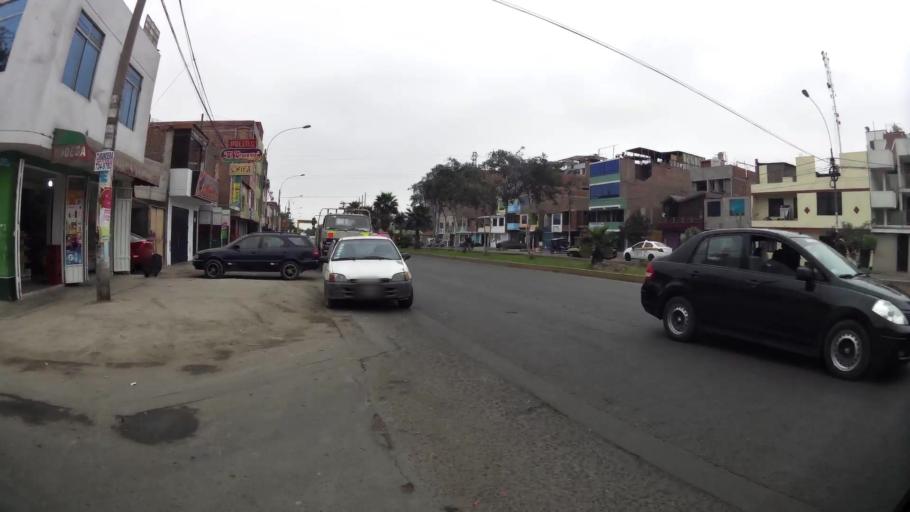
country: PE
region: Lima
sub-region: Lima
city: Independencia
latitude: -11.9688
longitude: -77.0796
